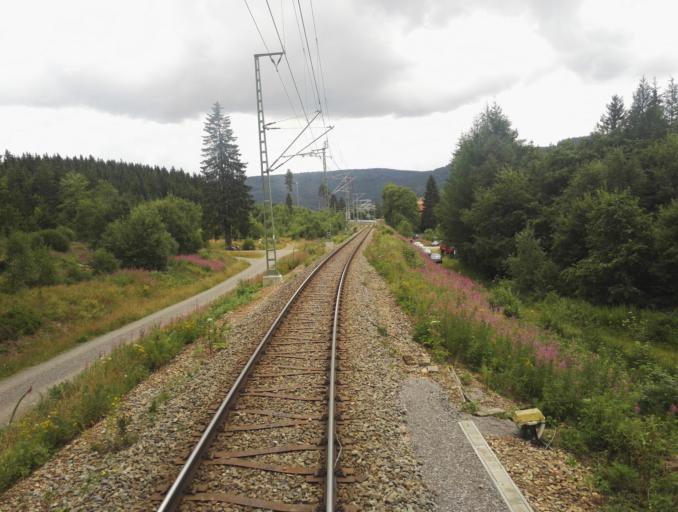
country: DE
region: Baden-Wuerttemberg
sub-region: Freiburg Region
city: Schluchsee
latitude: 47.8369
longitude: 8.1325
